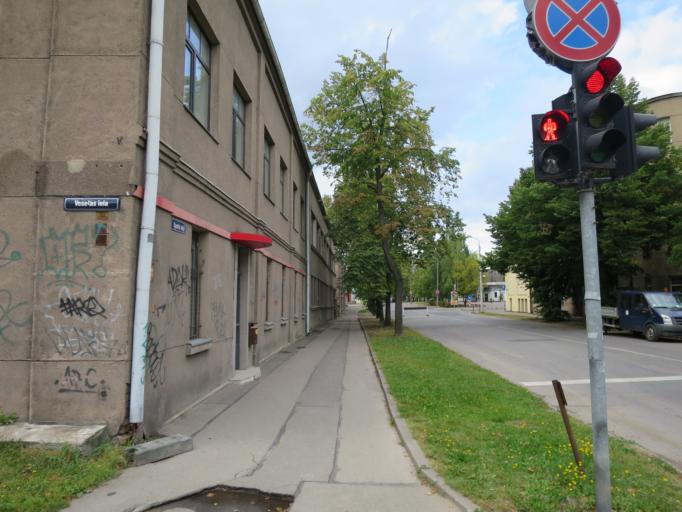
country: LV
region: Riga
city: Riga
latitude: 56.9628
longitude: 24.1201
